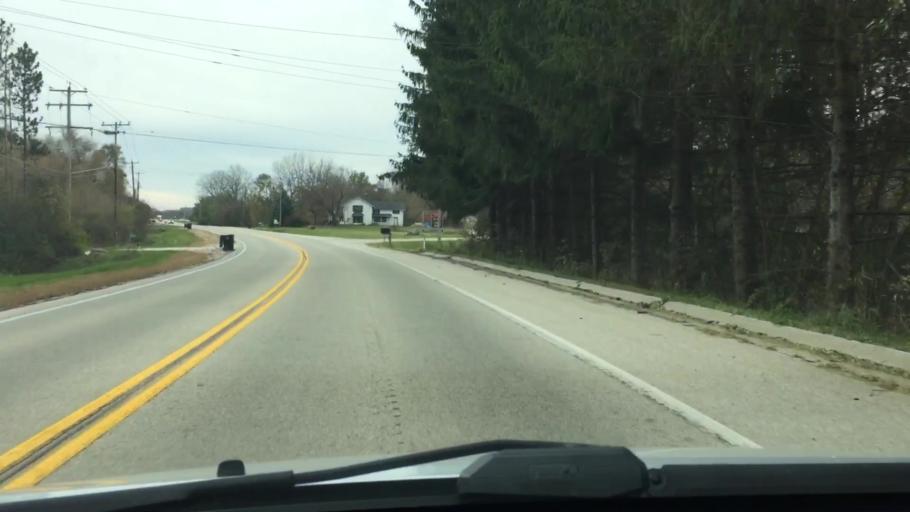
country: US
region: Wisconsin
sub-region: Waukesha County
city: Big Bend
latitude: 42.8973
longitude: -88.2717
